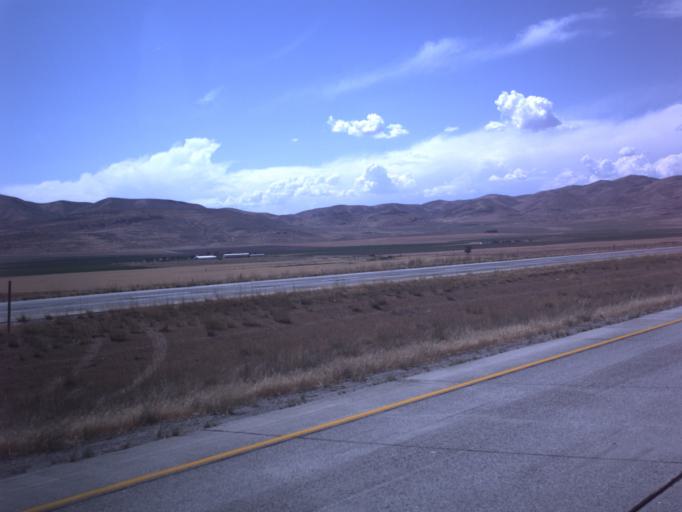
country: US
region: Utah
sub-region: Box Elder County
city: Tremonton
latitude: 41.7331
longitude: -112.2491
